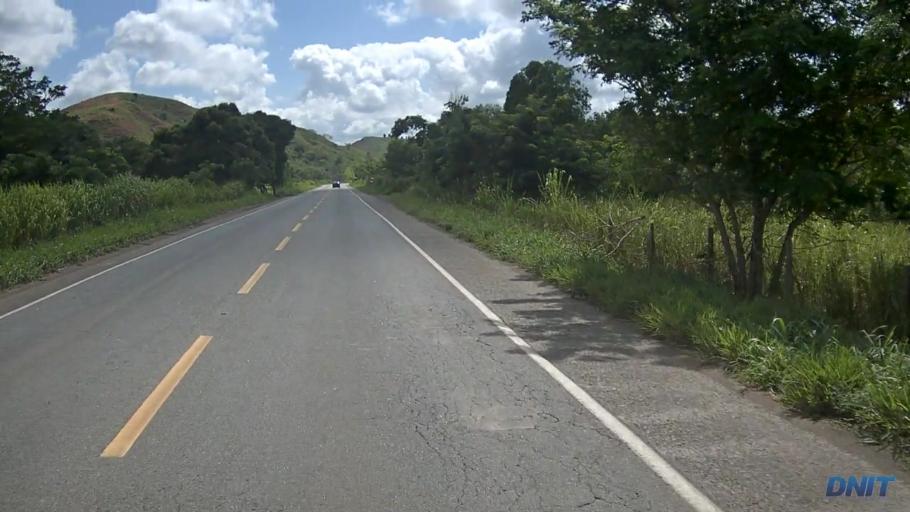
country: BR
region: Minas Gerais
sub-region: Belo Oriente
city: Belo Oriente
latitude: -19.1410
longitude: -42.2230
